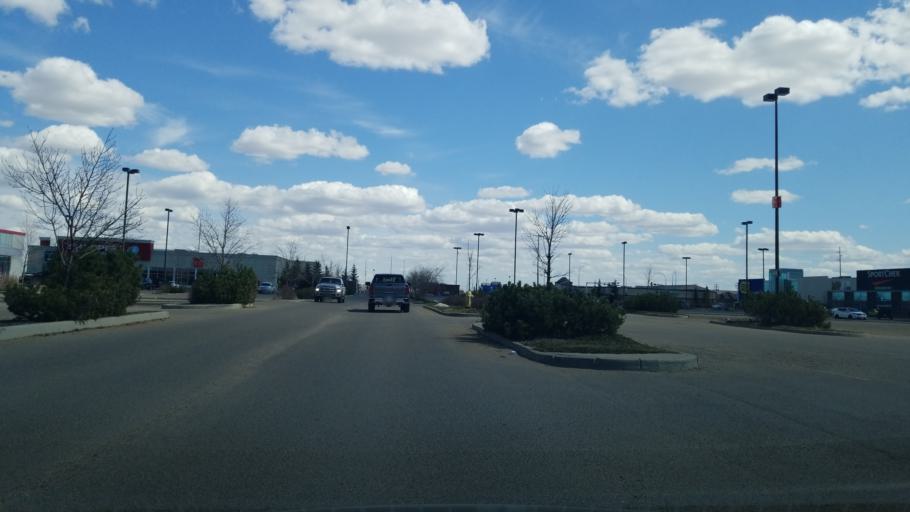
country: CA
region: Saskatchewan
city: Lloydminster
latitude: 53.2770
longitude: -110.0581
